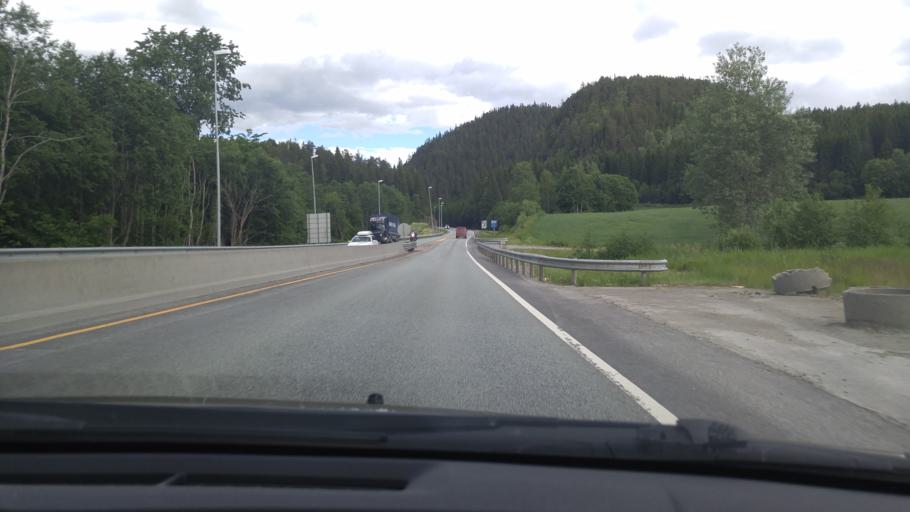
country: NO
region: Nord-Trondelag
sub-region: Steinkjer
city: Steinkjer
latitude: 64.0461
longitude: 11.4918
